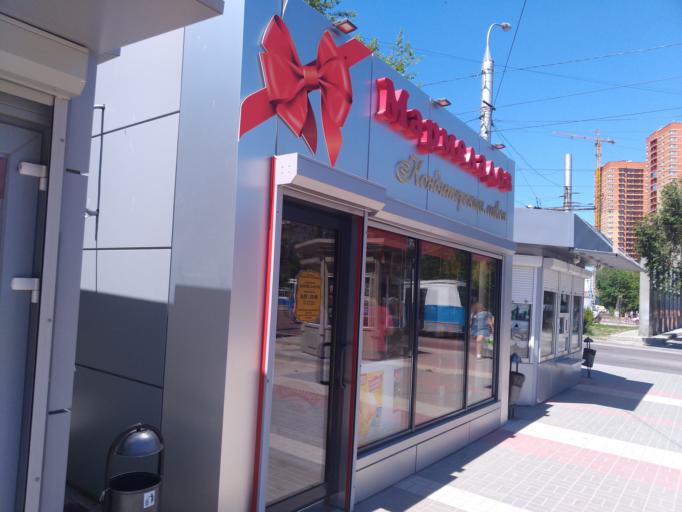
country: RU
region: Volgograd
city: Volgograd
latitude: 48.6772
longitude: 44.4736
